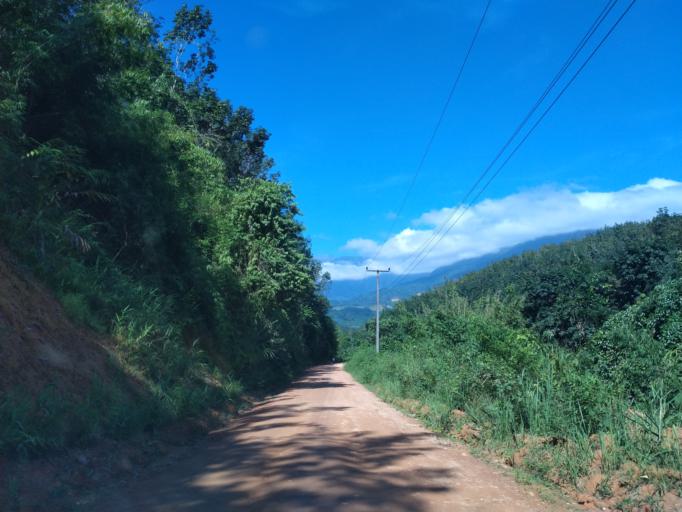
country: TH
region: Changwat Bueng Kan
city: Pak Khat
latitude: 18.6341
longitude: 103.0584
